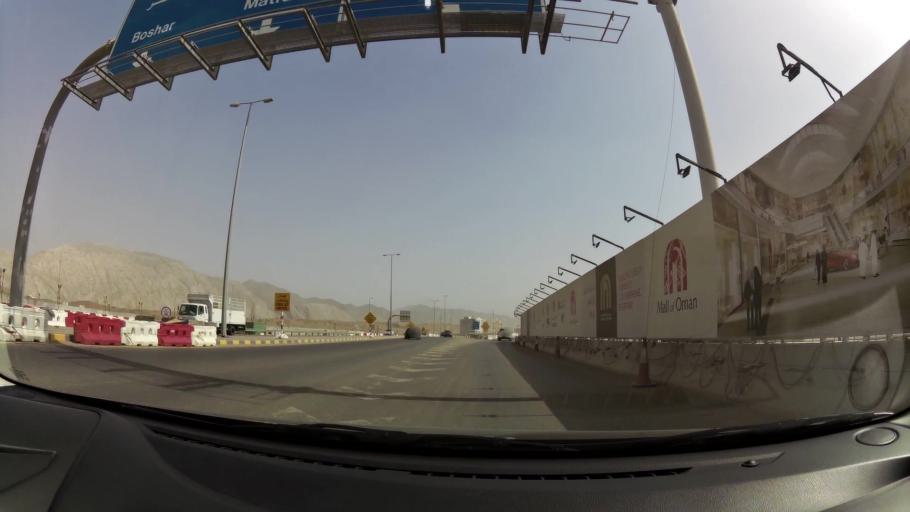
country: OM
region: Muhafazat Masqat
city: Bawshar
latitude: 23.5720
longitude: 58.4078
